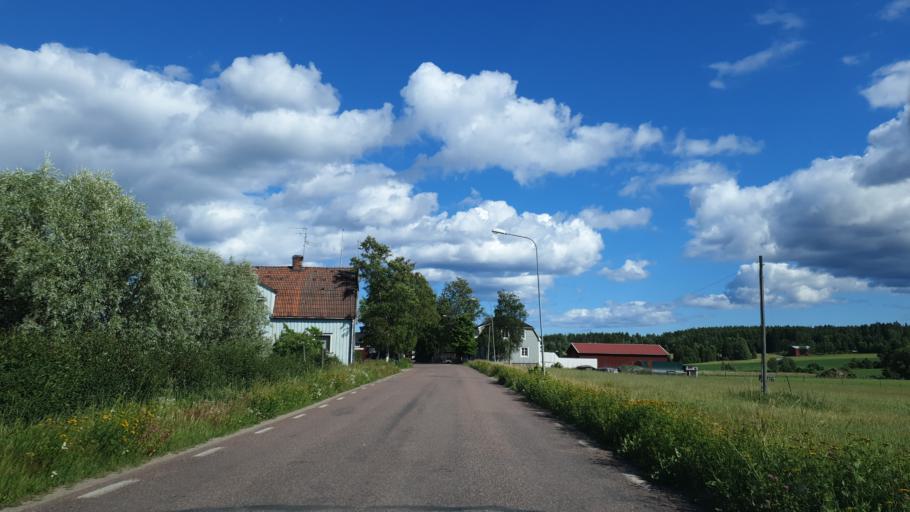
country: SE
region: Gaevleborg
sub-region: Nordanstigs Kommun
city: Bergsjoe
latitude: 62.0495
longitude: 17.2282
